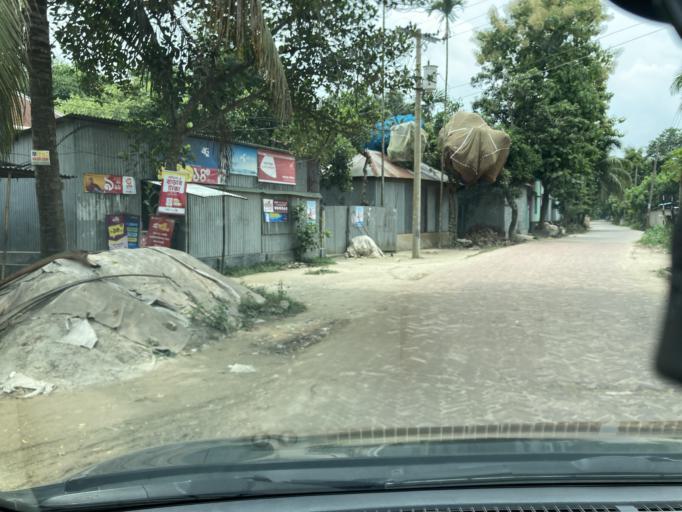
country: BD
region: Dhaka
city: Dohar
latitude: 23.8086
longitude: 90.0459
